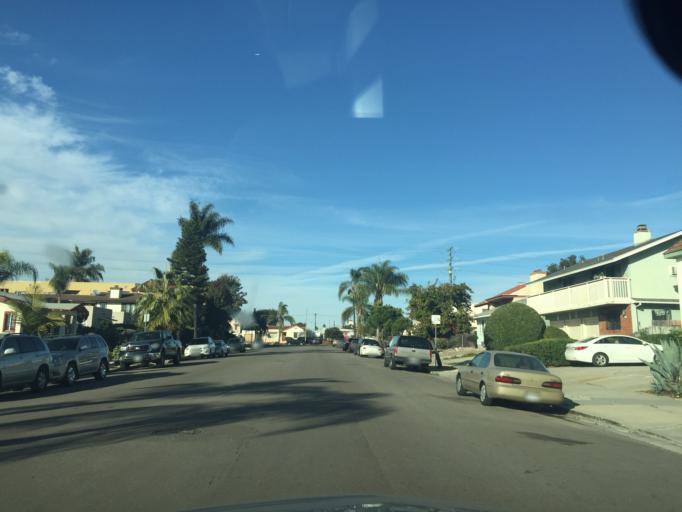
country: US
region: California
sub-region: San Diego County
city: San Diego
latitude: 32.7522
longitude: -117.1230
